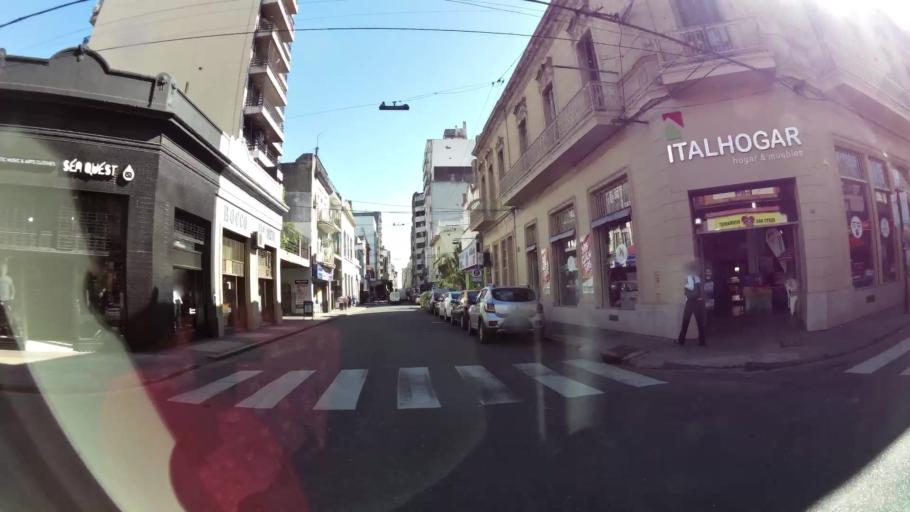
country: AR
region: Santa Fe
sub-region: Departamento de Rosario
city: Rosario
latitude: -32.9499
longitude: -60.6405
